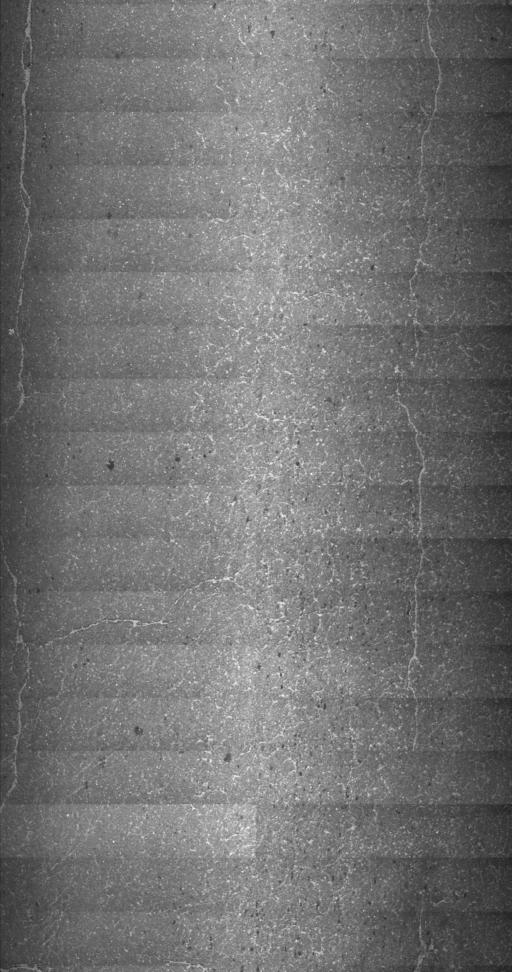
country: US
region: Vermont
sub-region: Caledonia County
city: Lyndonville
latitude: 44.8137
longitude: -71.8811
